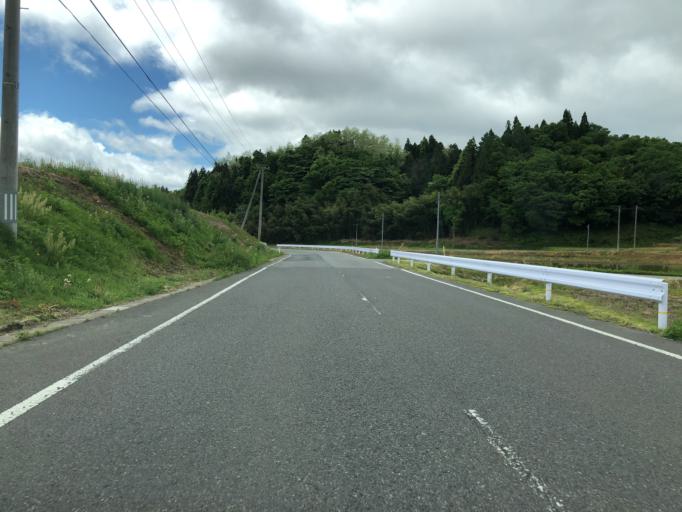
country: JP
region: Fukushima
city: Miharu
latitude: 37.4653
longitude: 140.4749
